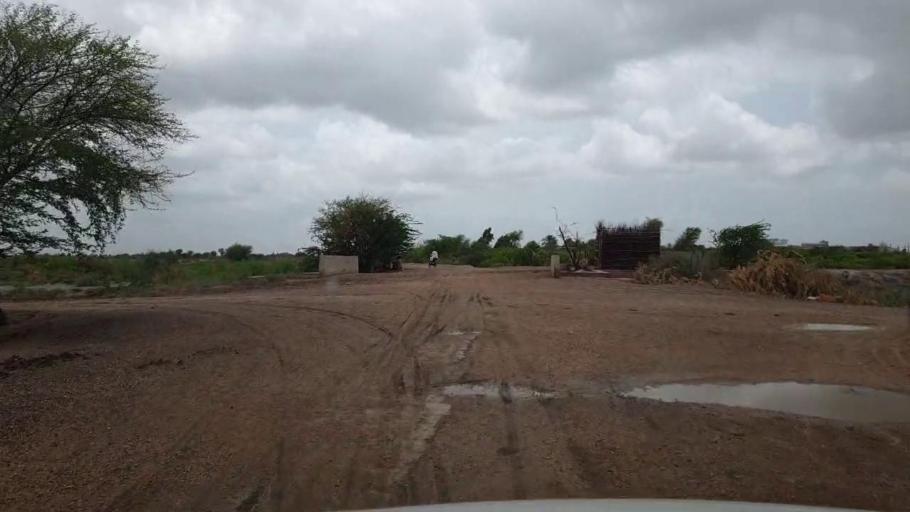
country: PK
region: Sindh
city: Kario
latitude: 24.7453
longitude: 68.5016
